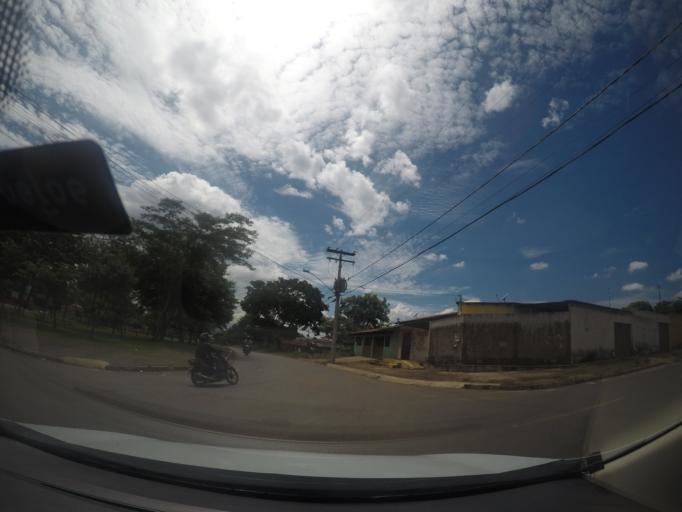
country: BR
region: Goias
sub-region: Goiania
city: Goiania
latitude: -16.6609
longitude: -49.3400
